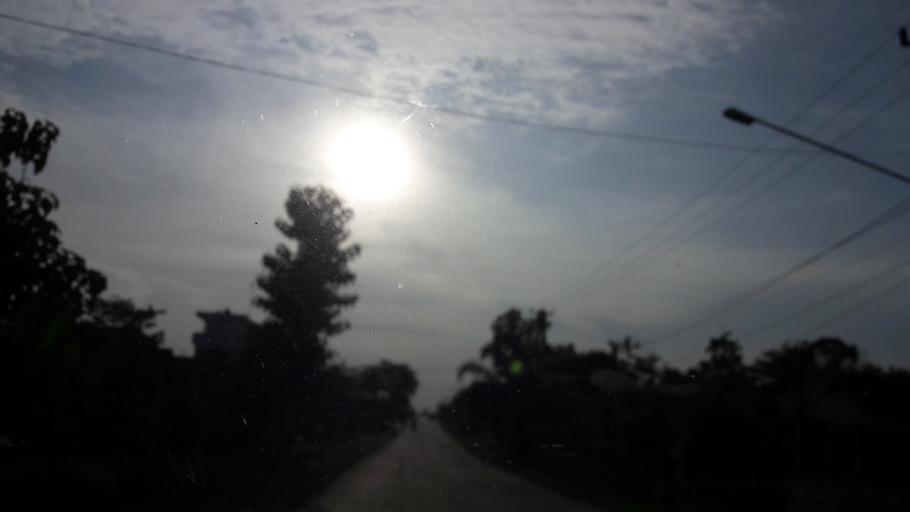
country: ID
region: South Sumatra
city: Gunungmegang Dalam
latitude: -3.3031
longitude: 103.8616
